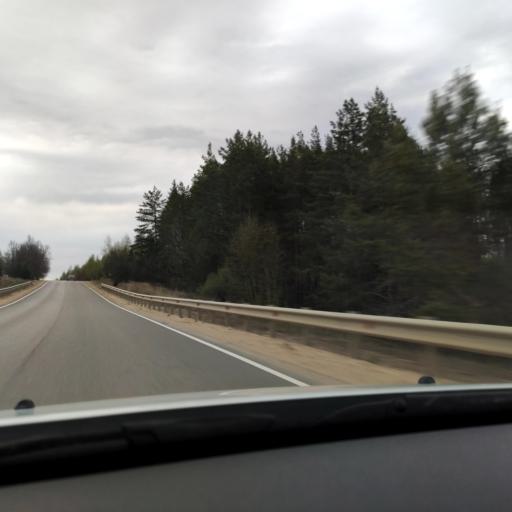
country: RU
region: Lipetsk
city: Zadonsk
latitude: 52.4242
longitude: 38.9511
